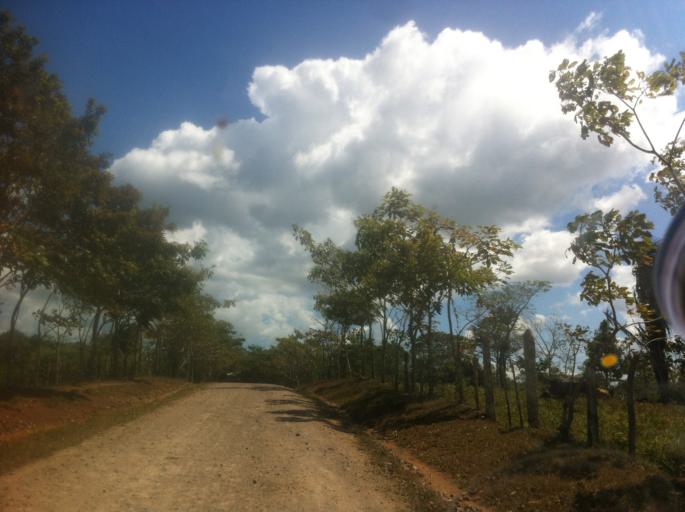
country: NI
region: Rio San Juan
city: San Carlos
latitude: 11.2385
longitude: -84.5276
